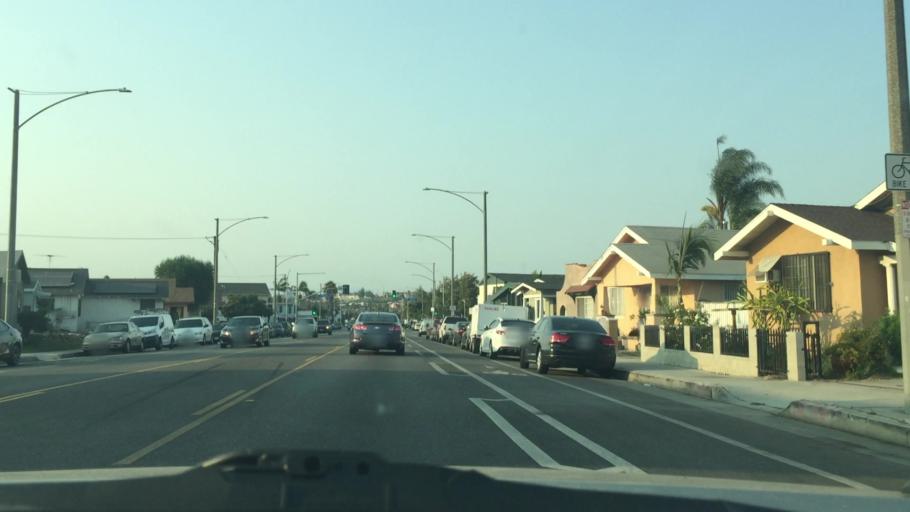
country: US
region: California
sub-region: Los Angeles County
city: Long Beach
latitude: 33.7849
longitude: -118.1773
